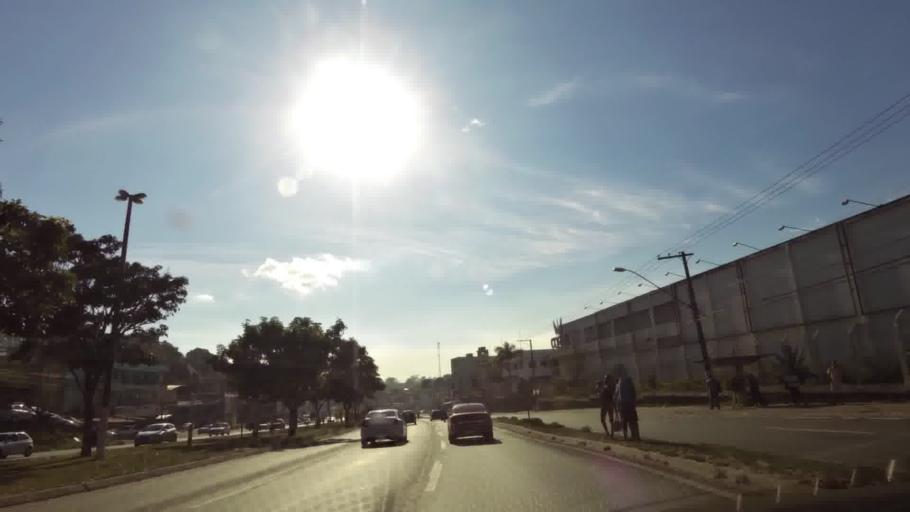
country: BR
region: Espirito Santo
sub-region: Vitoria
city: Vitoria
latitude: -20.3356
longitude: -40.3733
